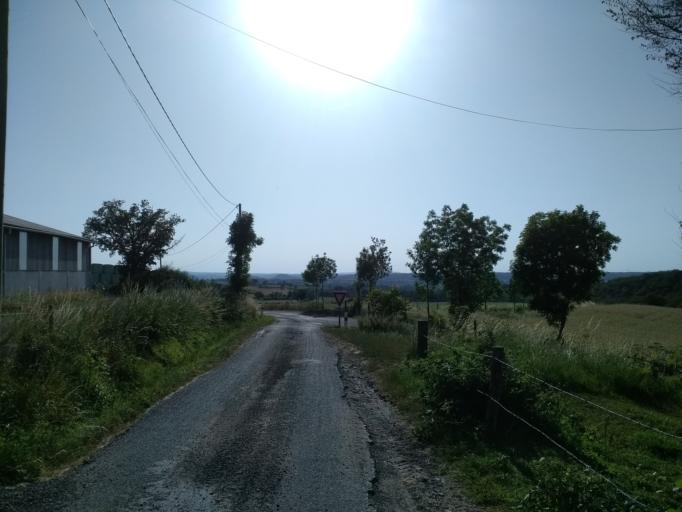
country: FR
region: Midi-Pyrenees
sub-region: Departement de l'Aveyron
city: La Loubiere
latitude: 44.3665
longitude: 2.6955
